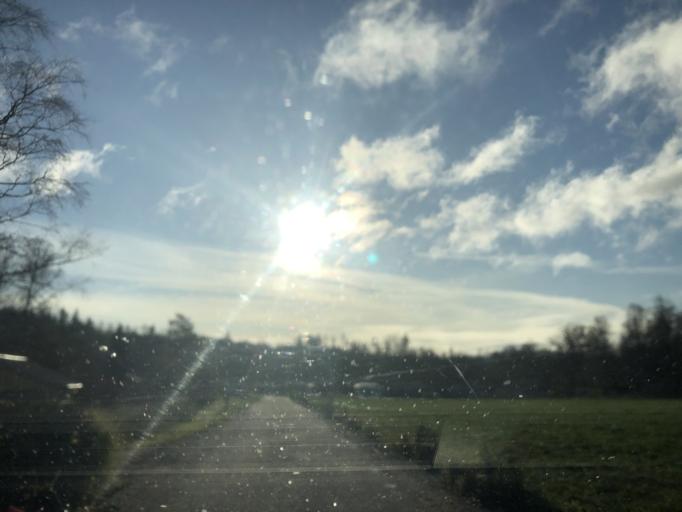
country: SE
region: Vaestra Goetaland
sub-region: Ulricehamns Kommun
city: Ulricehamn
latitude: 57.7223
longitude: 13.3980
